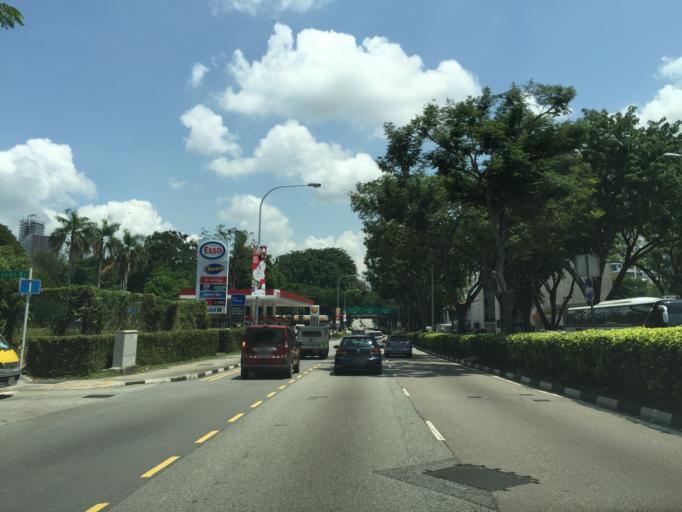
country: SG
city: Singapore
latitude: 1.3108
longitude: 103.8436
